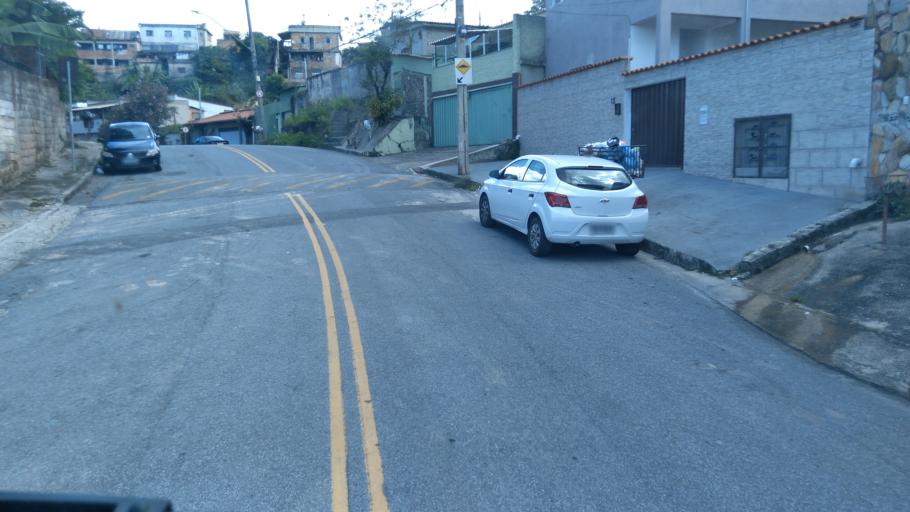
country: BR
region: Minas Gerais
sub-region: Belo Horizonte
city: Belo Horizonte
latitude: -19.8548
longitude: -43.9104
